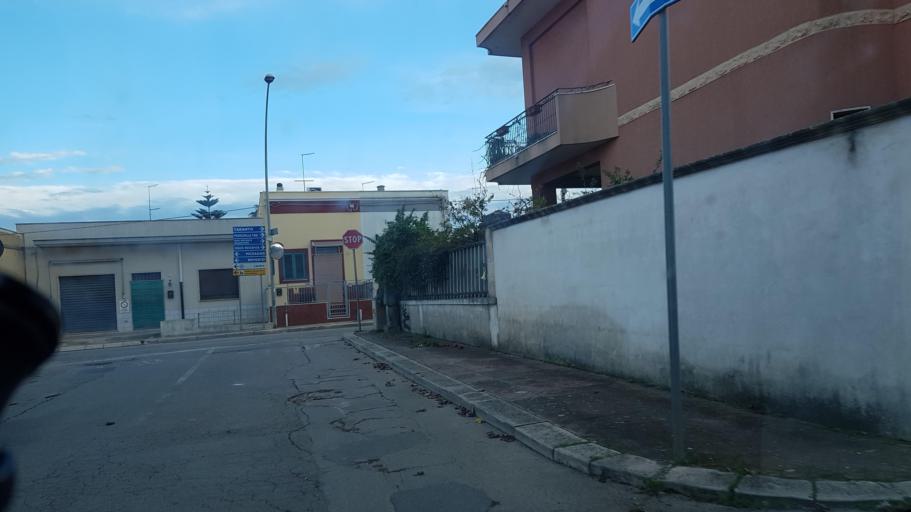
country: IT
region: Apulia
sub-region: Provincia di Brindisi
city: San Vito dei Normanni
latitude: 40.6530
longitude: 17.7008
